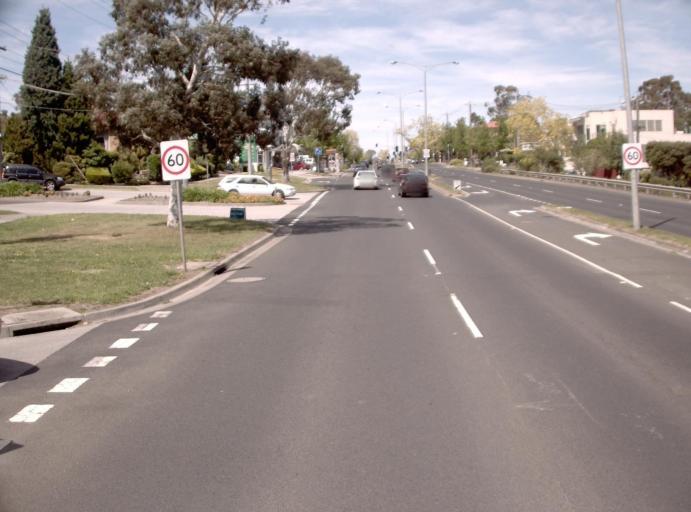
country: AU
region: Victoria
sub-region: Manningham
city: Donvale
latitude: -37.7798
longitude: 145.1637
